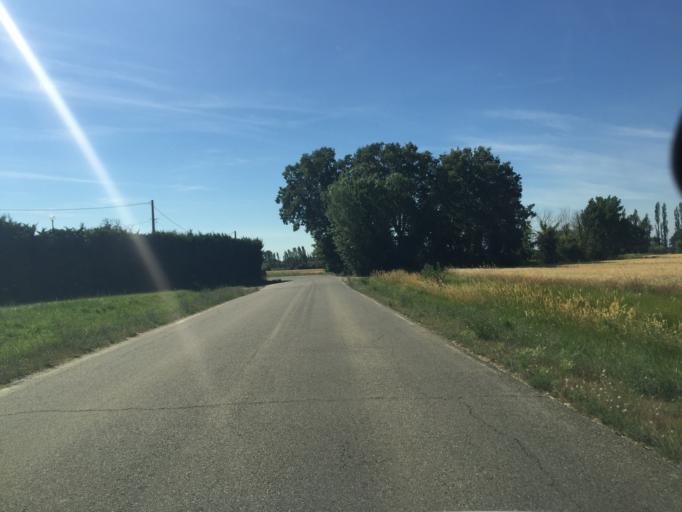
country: FR
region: Provence-Alpes-Cote d'Azur
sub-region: Departement du Vaucluse
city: Caderousse
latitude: 44.0901
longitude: 4.7793
